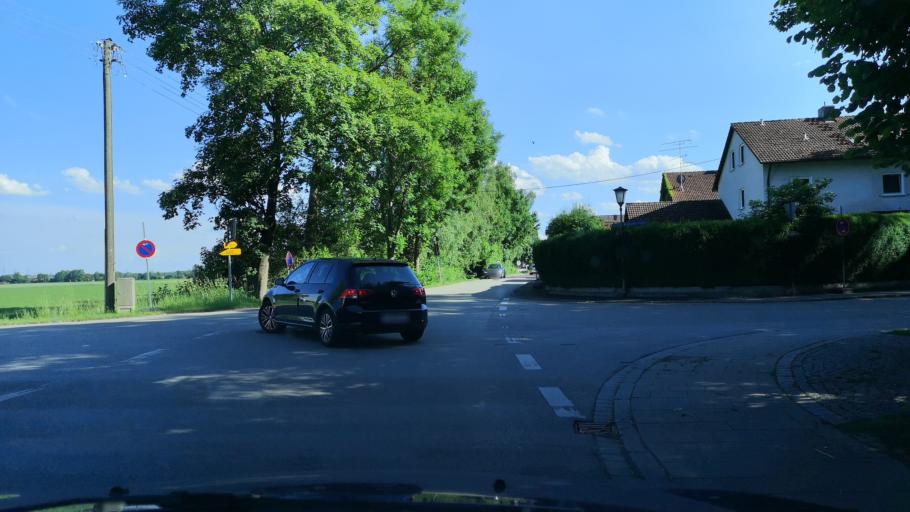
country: DE
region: Bavaria
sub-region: Upper Bavaria
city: Eichenried
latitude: 48.2450
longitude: 11.7804
